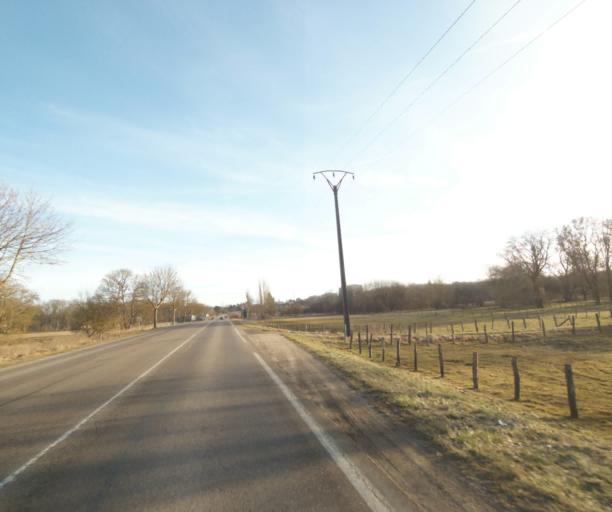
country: FR
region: Lorraine
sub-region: Departement de Meurthe-et-Moselle
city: Chavigny
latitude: 48.6410
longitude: 6.1334
